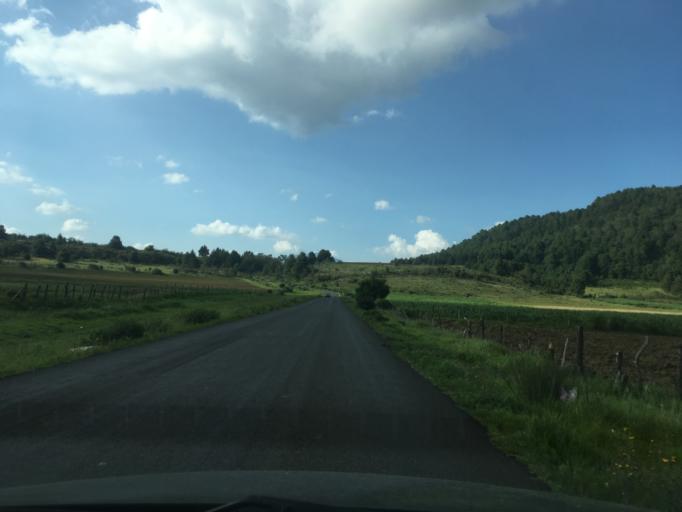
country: MX
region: Michoacan
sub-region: Nahuatzen
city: Sevina
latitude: 19.6255
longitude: -101.9278
